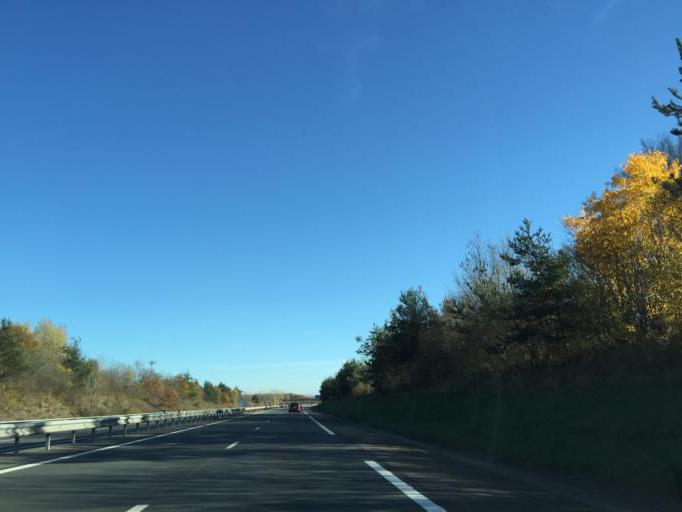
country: FR
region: Rhone-Alpes
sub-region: Departement de la Loire
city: Saint-Germain-Laval
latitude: 45.8506
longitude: 4.0712
